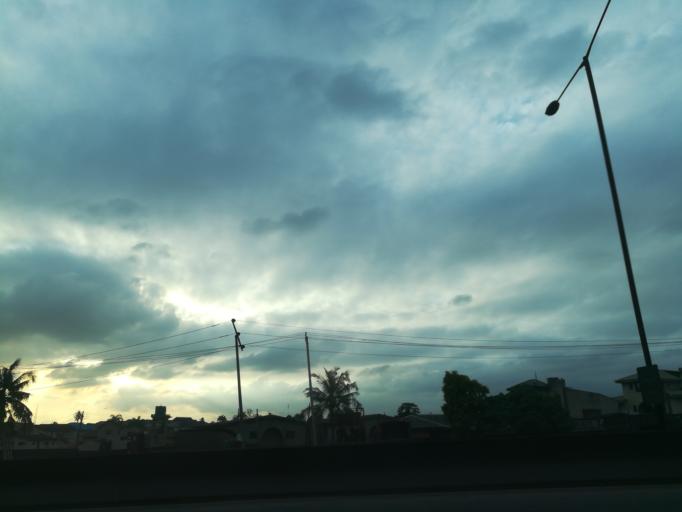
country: NG
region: Lagos
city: Ifako
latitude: 6.6334
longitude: 3.3661
